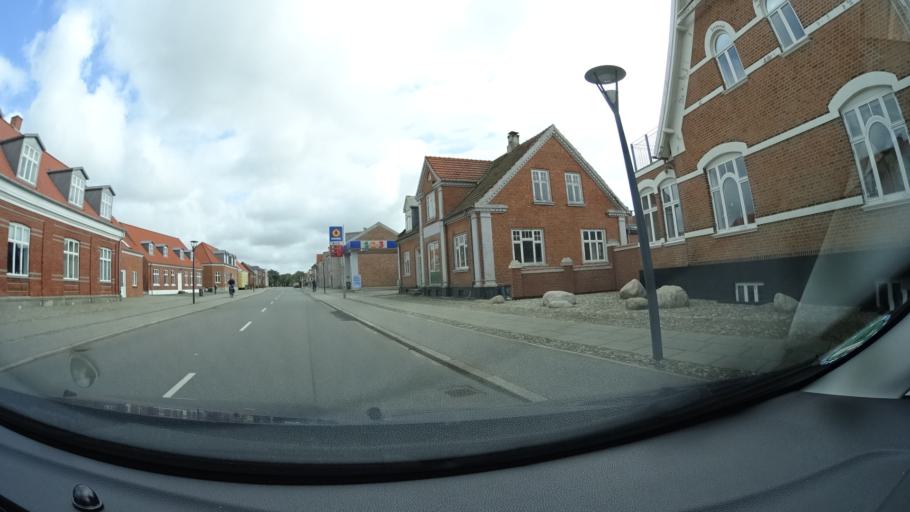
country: DK
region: Central Jutland
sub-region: Ringkobing-Skjern Kommune
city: Ringkobing
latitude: 56.0880
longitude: 8.2493
